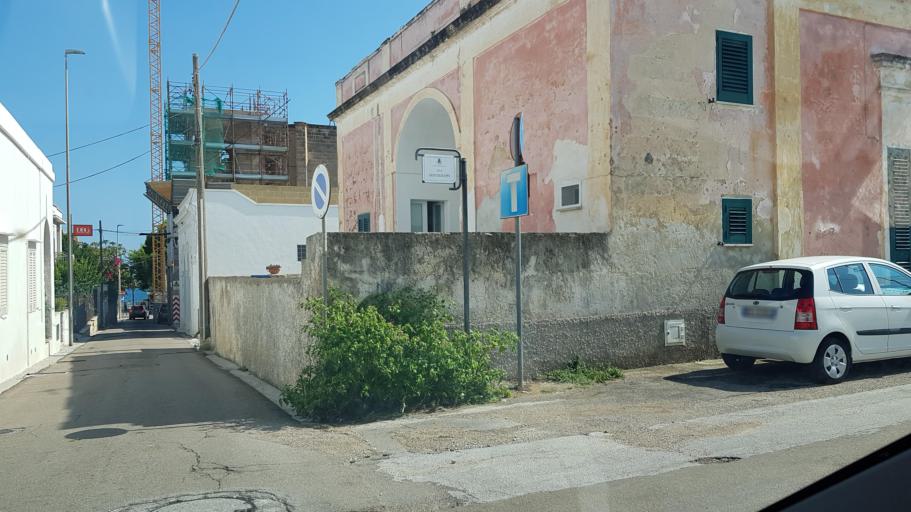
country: IT
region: Apulia
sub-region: Provincia di Lecce
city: Leuca
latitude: 39.7978
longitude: 18.3545
